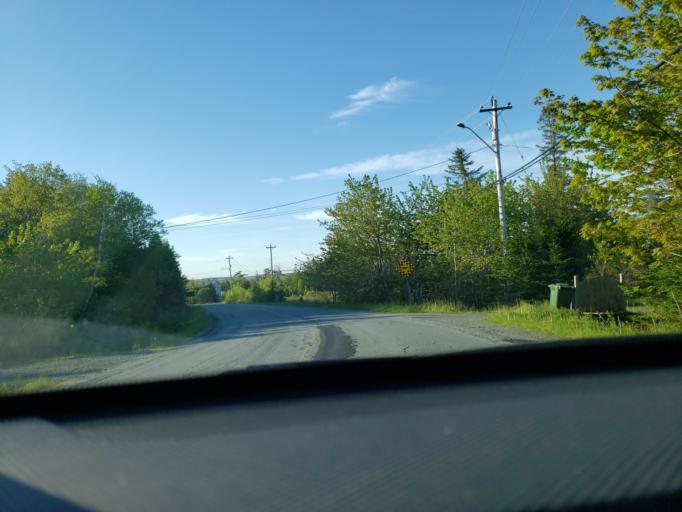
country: CA
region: Nova Scotia
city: Cole Harbour
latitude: 44.7207
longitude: -63.3993
